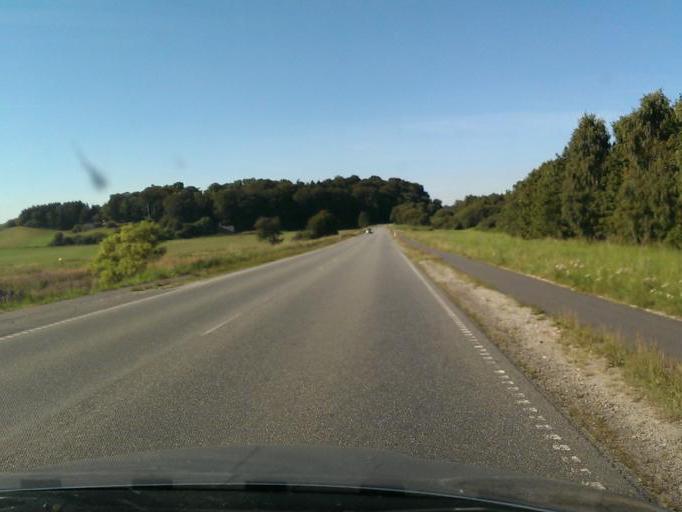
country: DK
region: Central Jutland
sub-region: Odder Kommune
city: Odder
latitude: 55.9354
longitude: 10.1526
